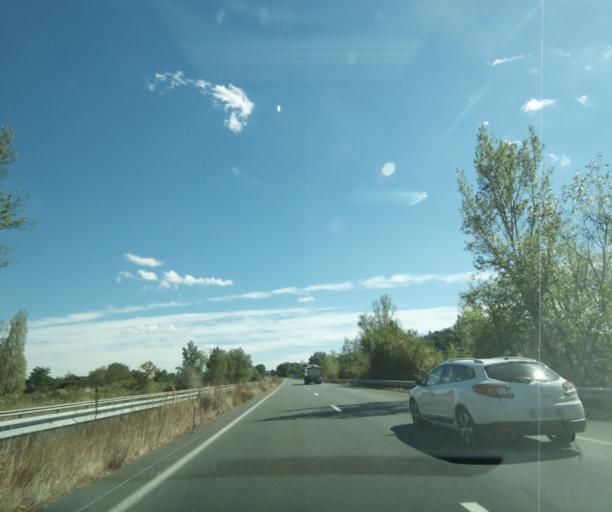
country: FR
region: Aquitaine
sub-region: Departement du Lot-et-Garonne
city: Buzet-sur-Baise
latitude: 44.2557
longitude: 0.2915
